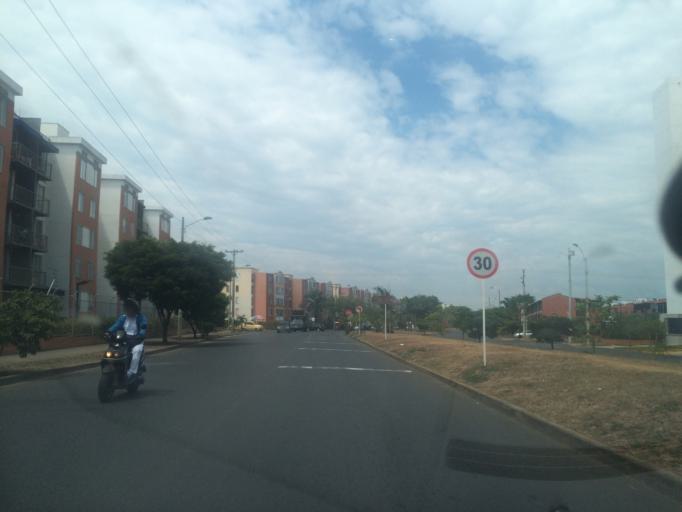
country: CO
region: Valle del Cauca
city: Cali
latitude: 3.3682
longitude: -76.5216
